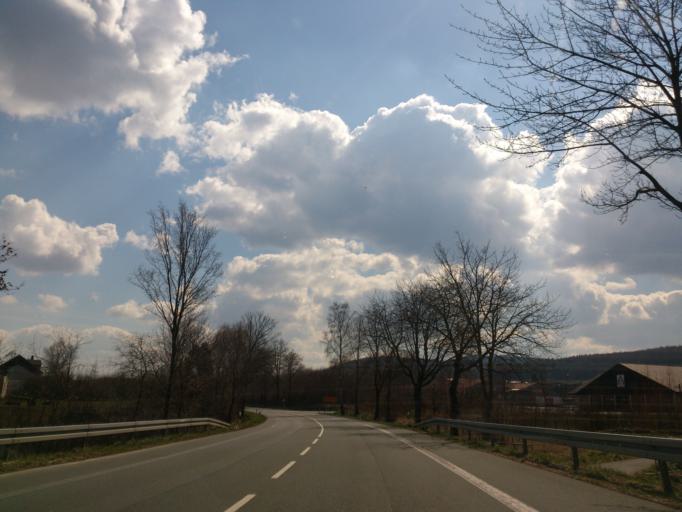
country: DE
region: North Rhine-Westphalia
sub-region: Regierungsbezirk Detmold
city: Willebadessen
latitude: 51.6263
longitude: 9.0242
